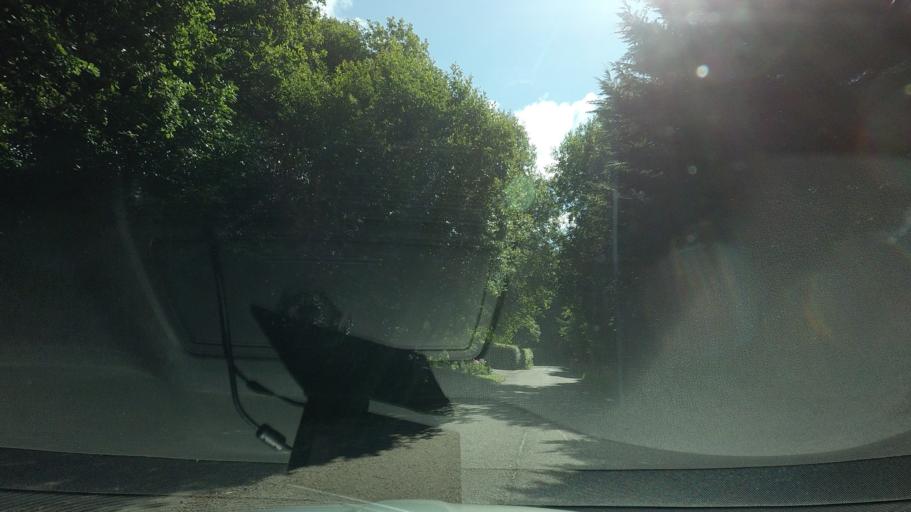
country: GB
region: Scotland
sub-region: Stirling
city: Killearn
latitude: 56.0644
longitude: -4.4674
